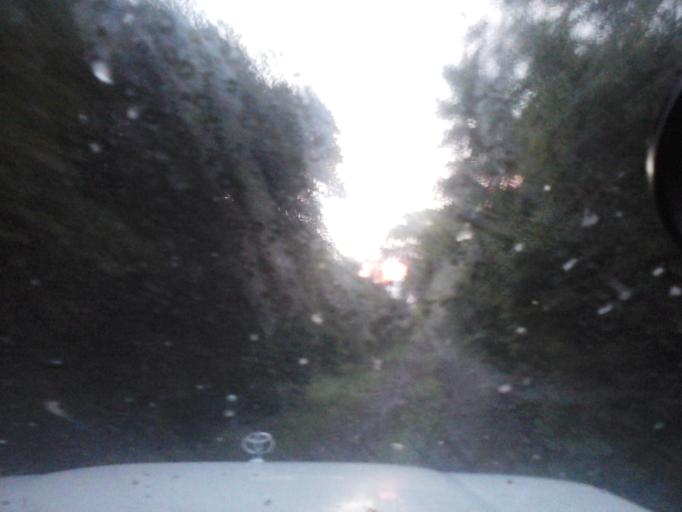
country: CO
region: Cesar
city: Agustin Codazzi
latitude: 10.1573
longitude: -73.2085
